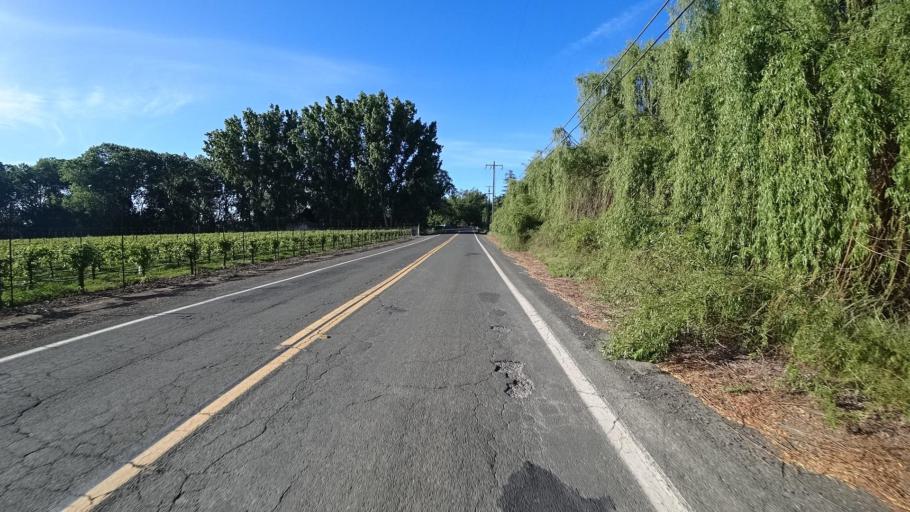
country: US
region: California
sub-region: Lake County
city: Lakeport
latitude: 39.0643
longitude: -122.9496
